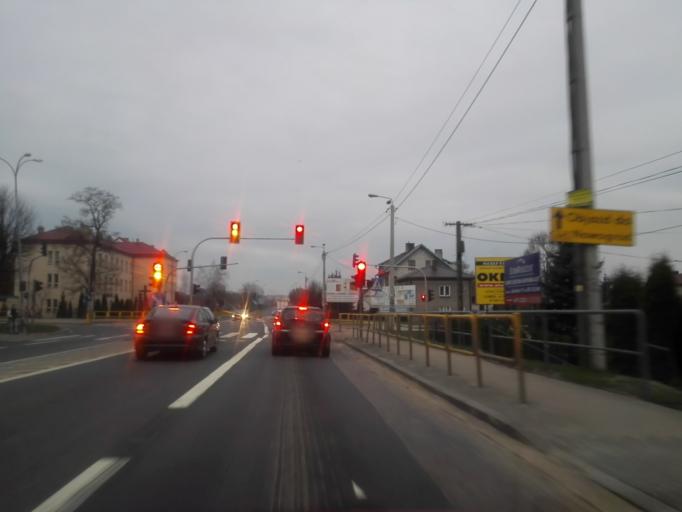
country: PL
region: Podlasie
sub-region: Powiat lomzynski
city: Piatnica
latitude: 53.1957
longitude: 22.0958
